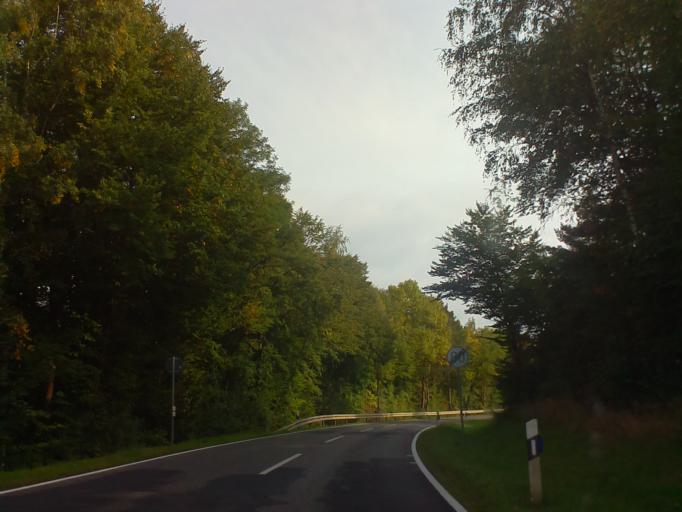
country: DE
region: Hesse
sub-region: Regierungsbezirk Kassel
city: Schenklengsfeld
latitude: 50.8407
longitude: 9.8312
